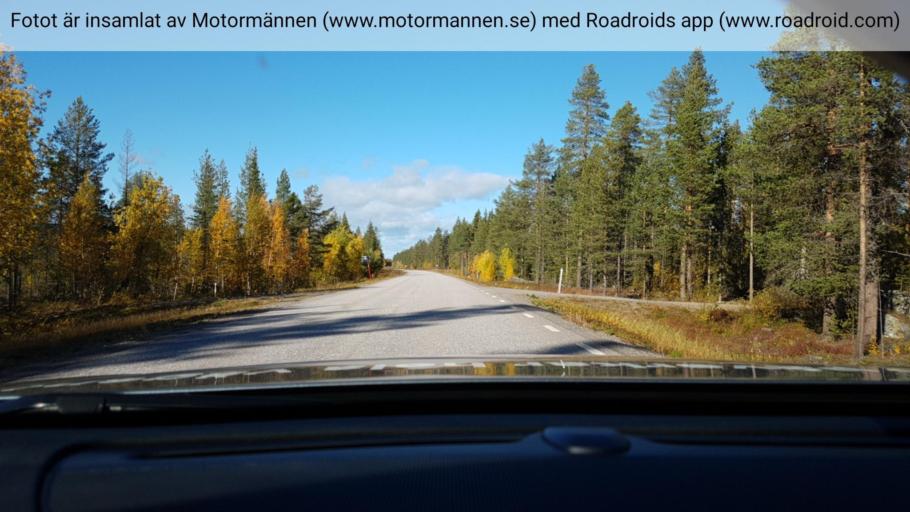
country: SE
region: Norrbotten
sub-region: Arvidsjaurs Kommun
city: Arvidsjaur
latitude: 65.6795
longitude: 18.8224
